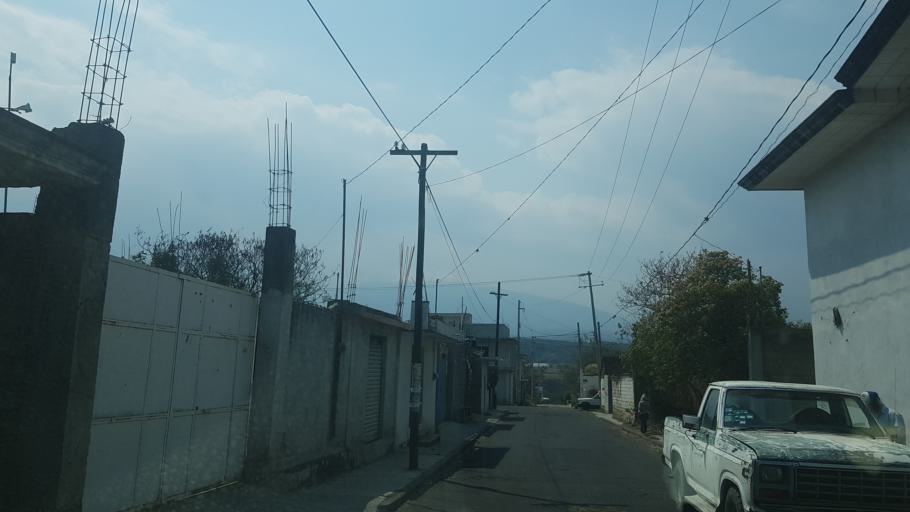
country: MX
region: Puebla
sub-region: Tianguismanalco
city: San Martin Tlapala
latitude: 18.9746
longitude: -98.4517
